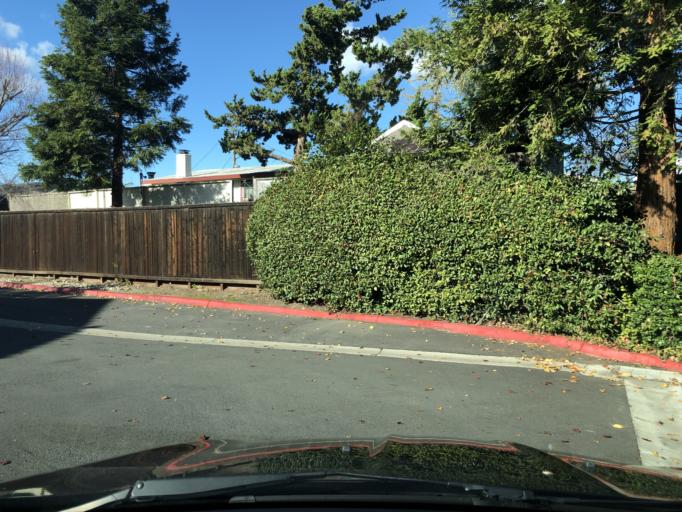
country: US
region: California
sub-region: Contra Costa County
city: Pacheco
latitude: 37.9845
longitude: -122.0707
